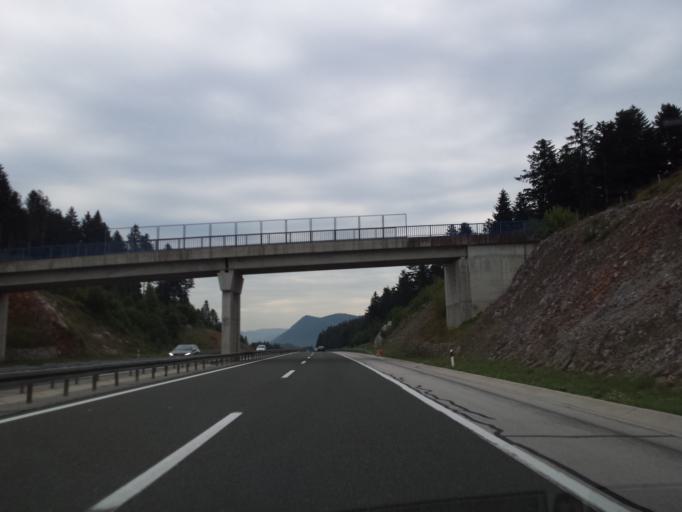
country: HR
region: Licko-Senjska
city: Otocac
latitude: 44.8497
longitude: 15.2313
